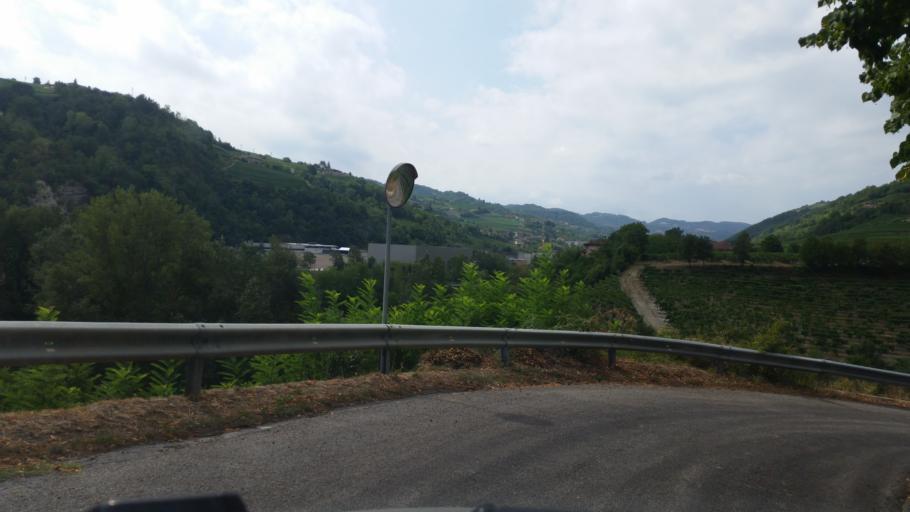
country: IT
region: Piedmont
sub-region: Provincia di Cuneo
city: Camo
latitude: 44.6859
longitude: 8.1994
